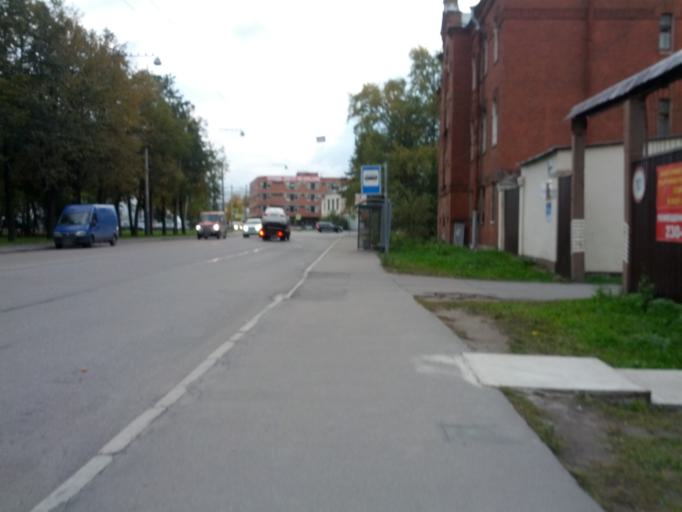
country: RU
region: Leningrad
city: Krestovskiy ostrov
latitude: 59.9605
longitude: 30.2709
